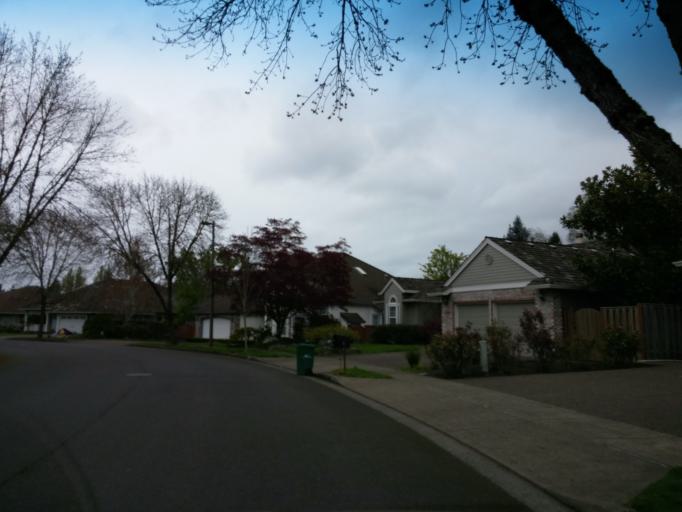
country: US
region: Oregon
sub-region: Washington County
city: Oak Hills
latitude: 45.5242
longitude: -122.8484
